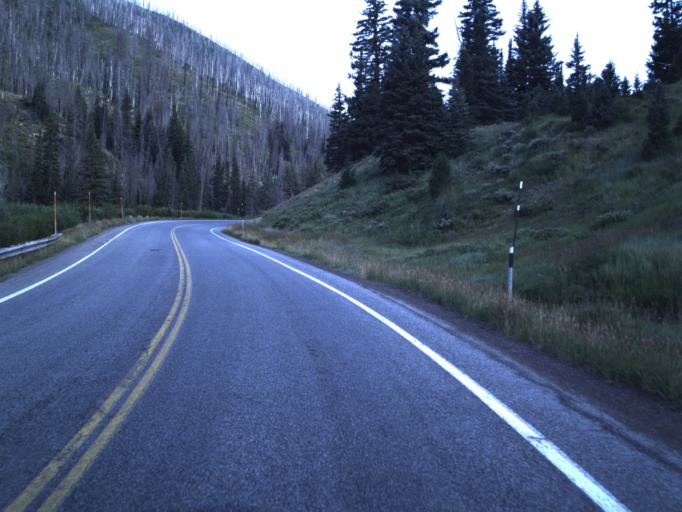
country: US
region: Utah
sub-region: Sanpete County
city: Fairview
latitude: 39.5632
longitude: -111.1760
